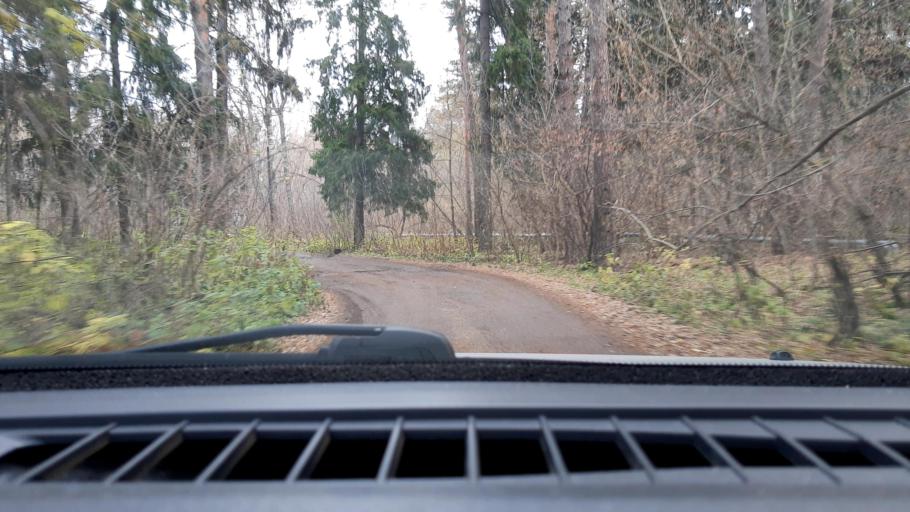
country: RU
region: Nizjnij Novgorod
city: Kstovo
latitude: 56.1692
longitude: 44.1275
